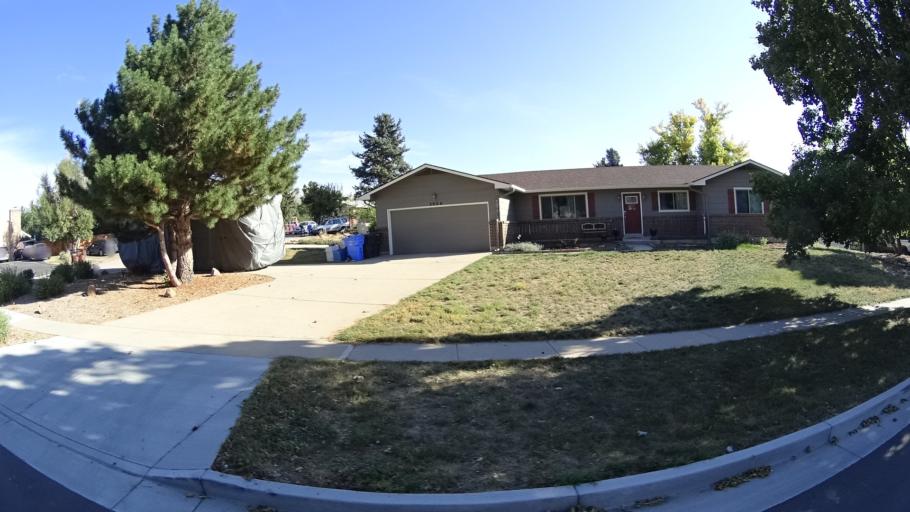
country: US
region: Colorado
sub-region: El Paso County
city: Cimarron Hills
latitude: 38.9068
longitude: -104.7608
